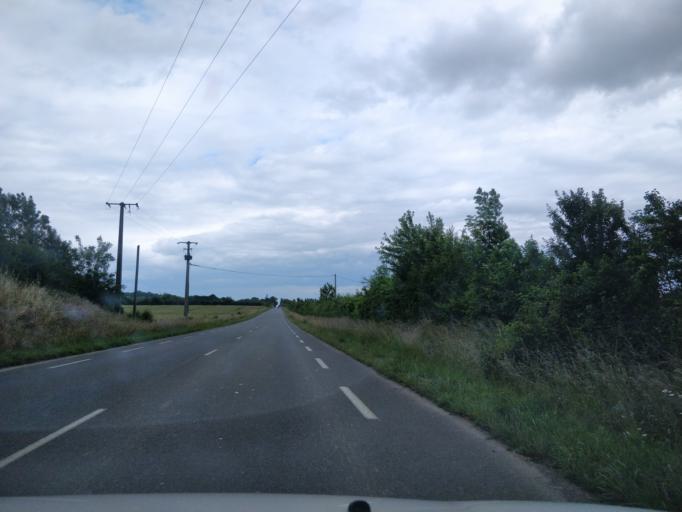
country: FR
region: Pays de la Loire
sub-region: Departement de Maine-et-Loire
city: Grez-Neuville
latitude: 47.6362
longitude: -0.6773
